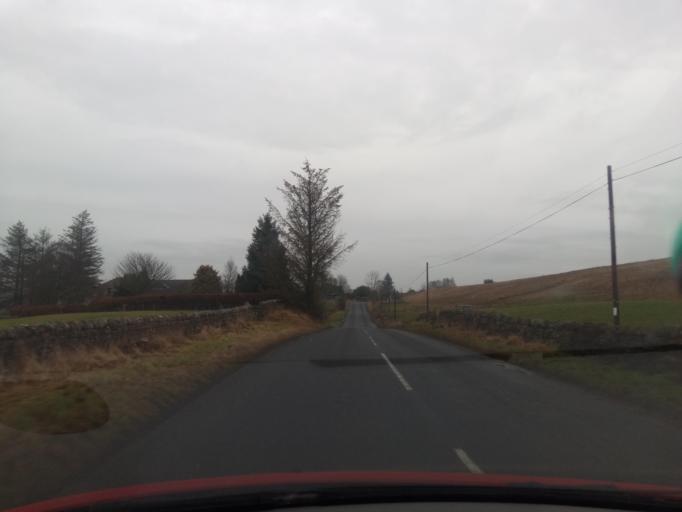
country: GB
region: England
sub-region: Northumberland
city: Rochester
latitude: 55.1669
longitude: -2.3765
